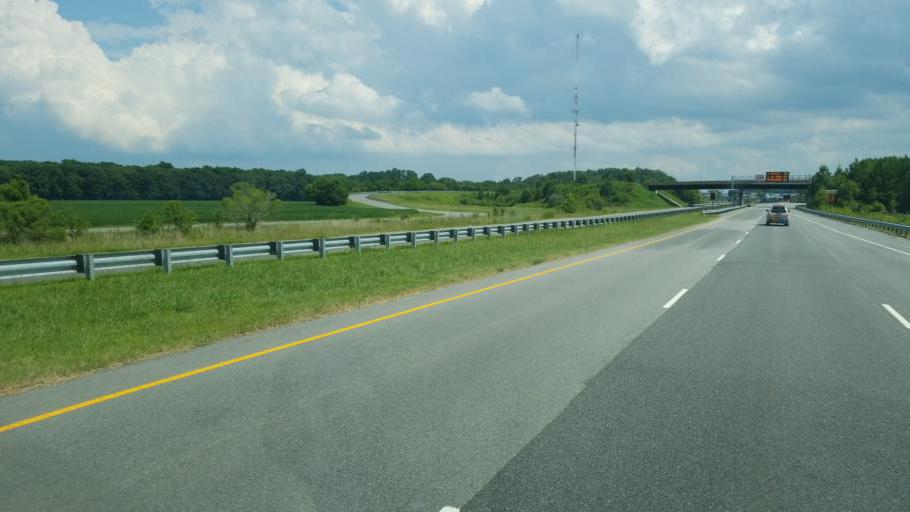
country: US
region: North Carolina
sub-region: Currituck County
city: Moyock
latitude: 36.6138
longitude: -76.2090
